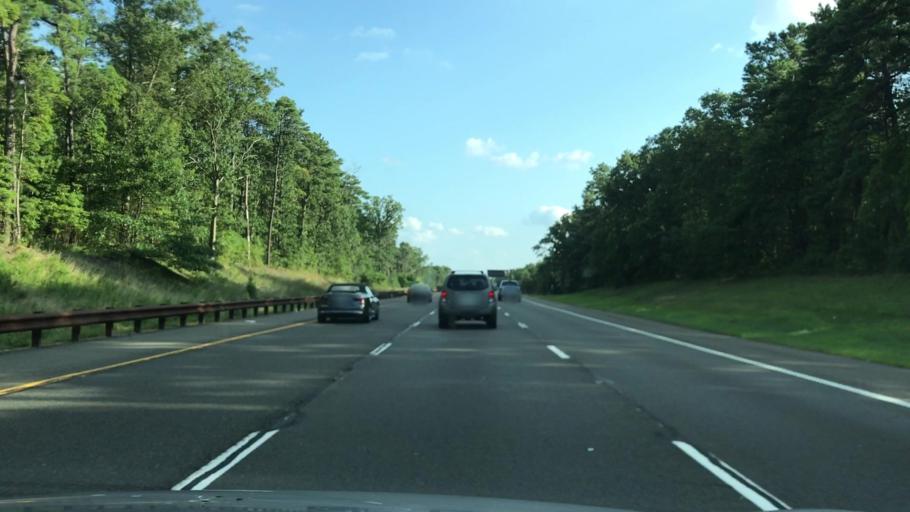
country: US
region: New Jersey
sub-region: Ocean County
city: South Toms River
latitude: 39.8986
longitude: -74.2122
